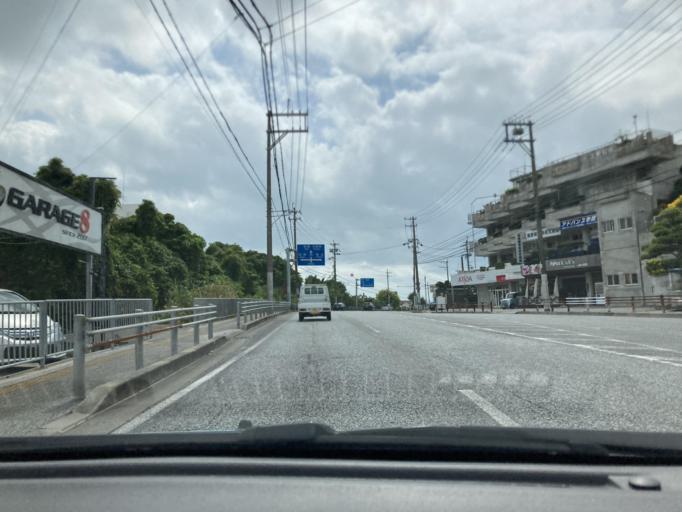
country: JP
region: Okinawa
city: Okinawa
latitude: 26.3220
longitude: 127.8217
